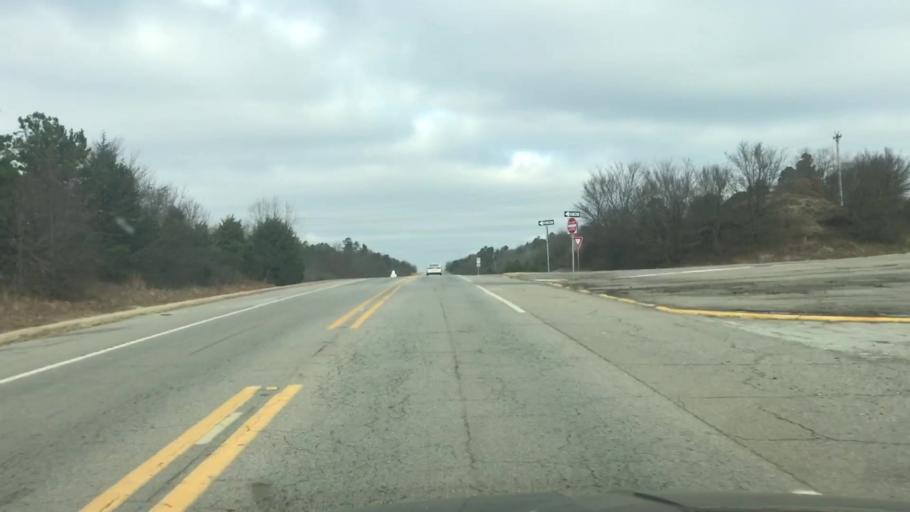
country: US
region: Arkansas
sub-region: Scott County
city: Waldron
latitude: 34.8561
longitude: -94.0671
